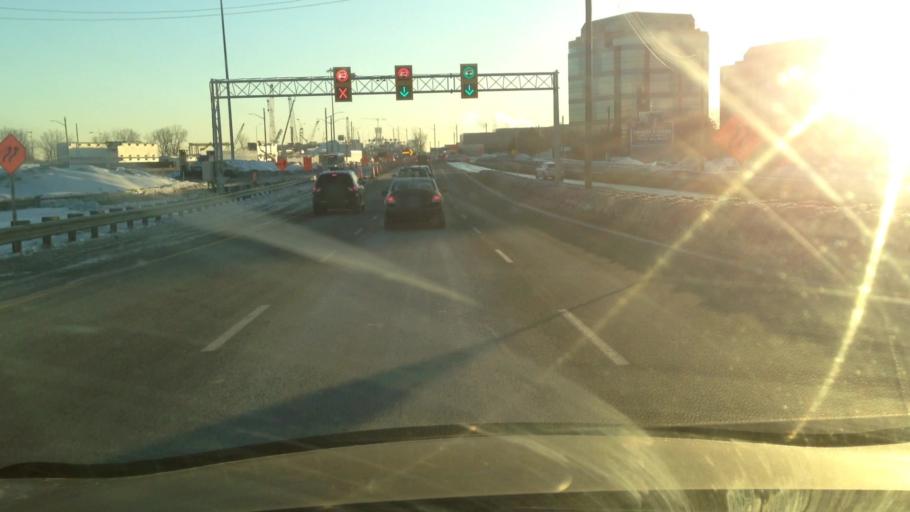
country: CA
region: Quebec
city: Westmount
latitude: 45.4701
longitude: -73.5426
